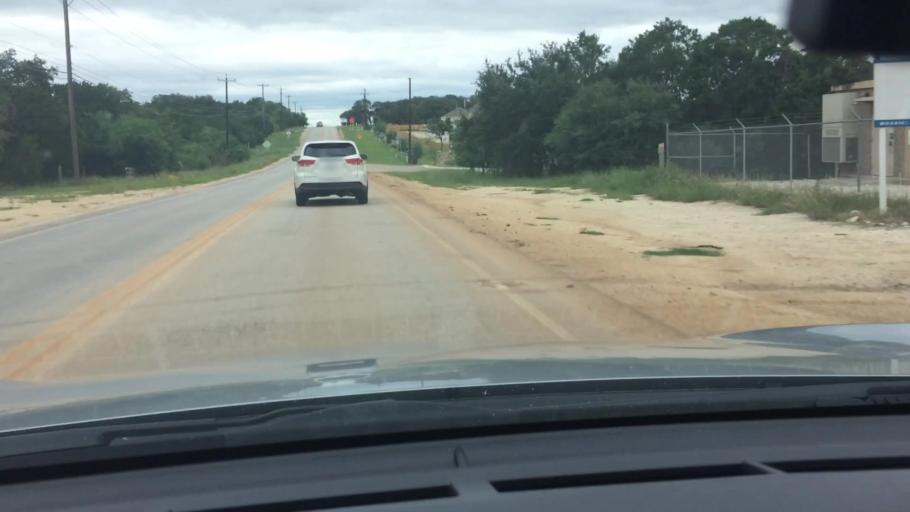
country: US
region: Texas
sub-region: Comal County
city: Garden Ridge
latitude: 29.6388
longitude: -98.3772
